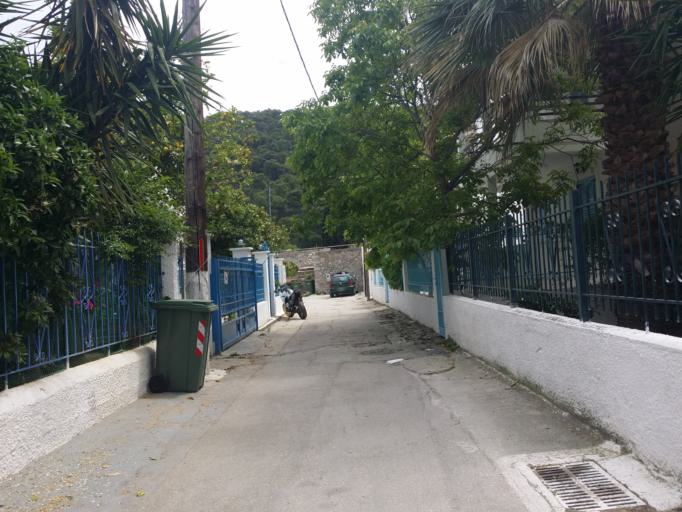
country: GR
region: Attica
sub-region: Nomos Piraios
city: Poros
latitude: 37.5093
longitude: 23.4725
